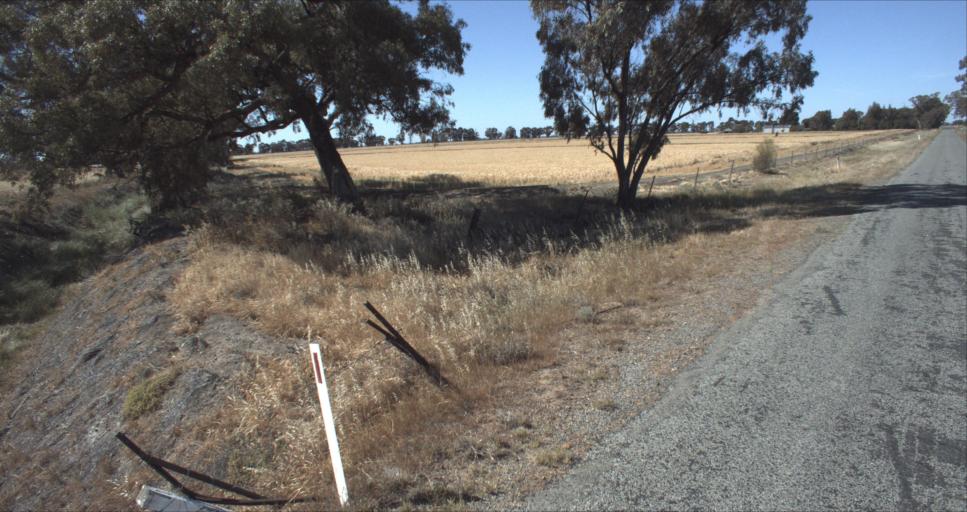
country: AU
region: New South Wales
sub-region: Leeton
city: Leeton
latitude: -34.5406
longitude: 146.3165
